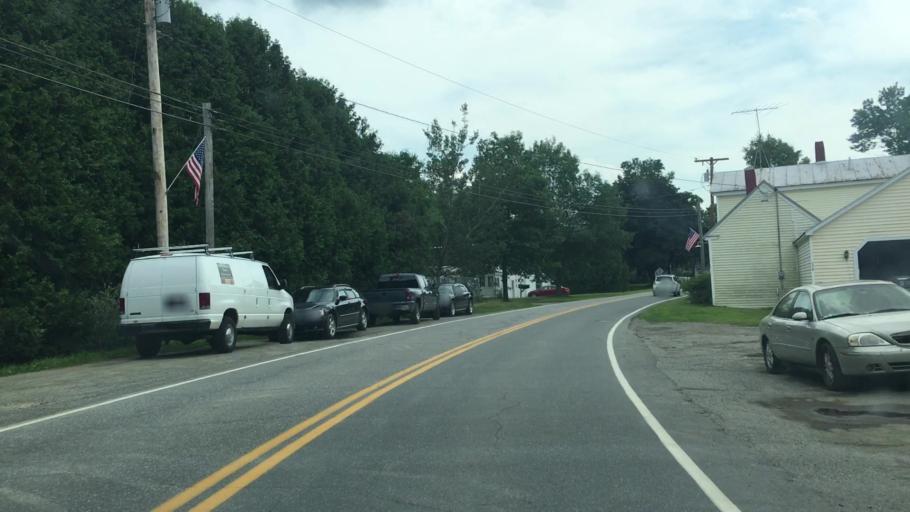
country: US
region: Maine
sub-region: Kennebec County
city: Vassalboro
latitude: 44.4505
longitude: -69.6064
